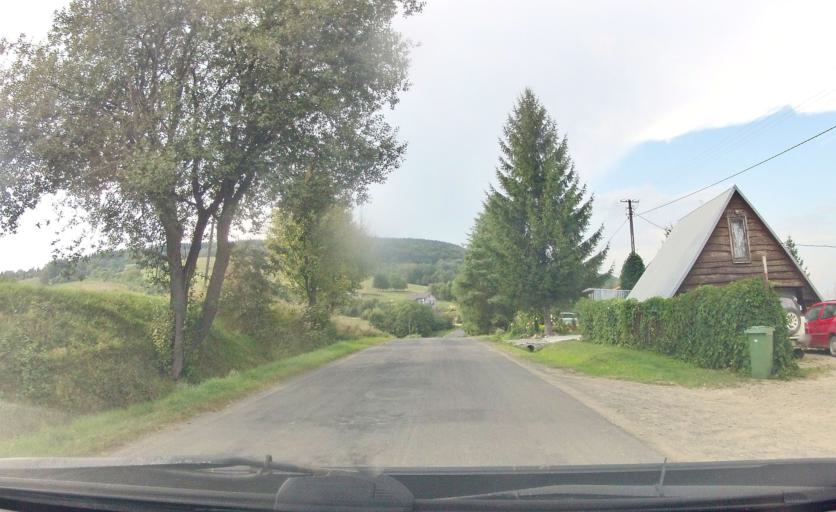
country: PL
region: Subcarpathian Voivodeship
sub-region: Powiat krosnienski
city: Dukla
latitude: 49.5211
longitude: 21.6174
